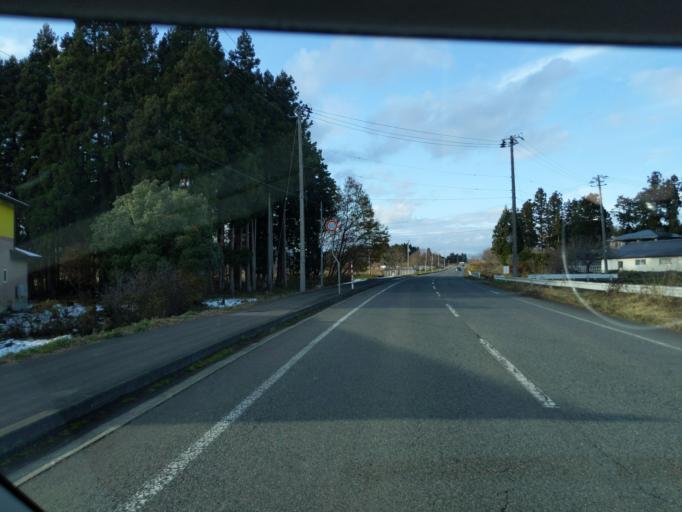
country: JP
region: Iwate
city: Mizusawa
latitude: 39.1914
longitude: 141.0733
